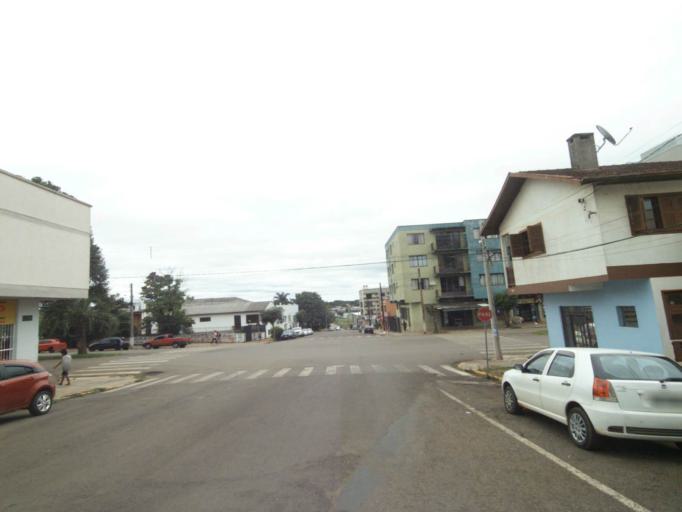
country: BR
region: Rio Grande do Sul
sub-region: Lagoa Vermelha
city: Lagoa Vermelha
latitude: -28.2122
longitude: -51.5212
